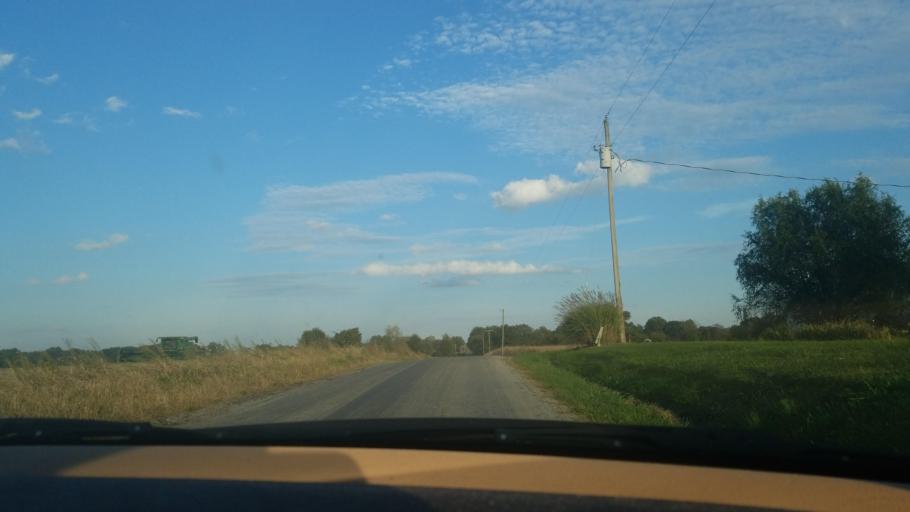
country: US
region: Illinois
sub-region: Saline County
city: Carrier Mills
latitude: 37.8050
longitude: -88.6786
